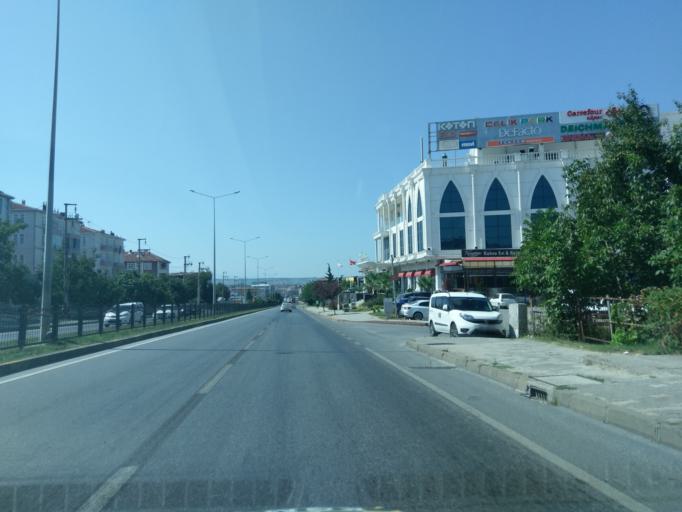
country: TR
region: Samsun
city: Bafra
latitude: 41.5565
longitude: 35.9105
